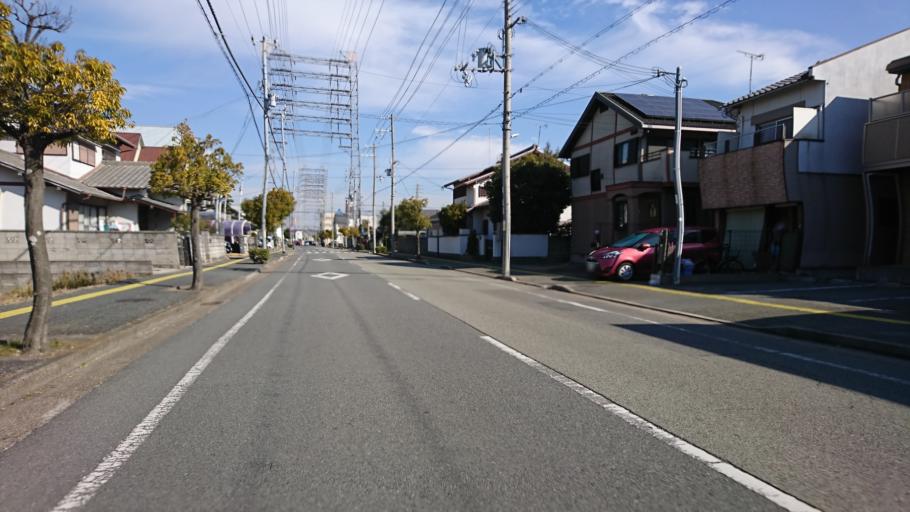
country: JP
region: Hyogo
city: Kakogawacho-honmachi
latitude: 34.7567
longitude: 134.8007
